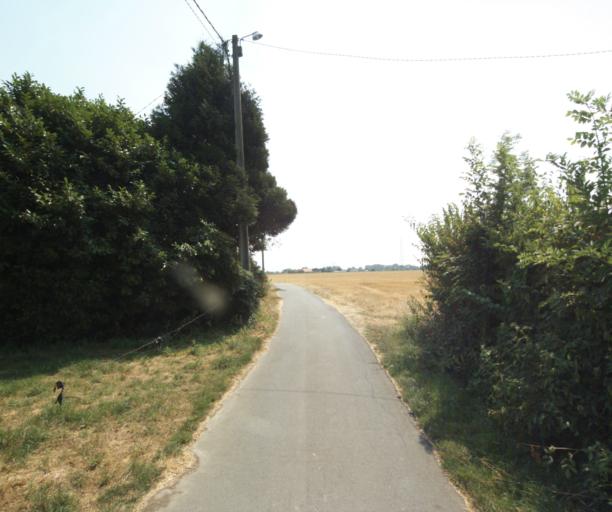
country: FR
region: Nord-Pas-de-Calais
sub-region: Departement du Nord
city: Wambrechies
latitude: 50.7027
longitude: 3.0399
